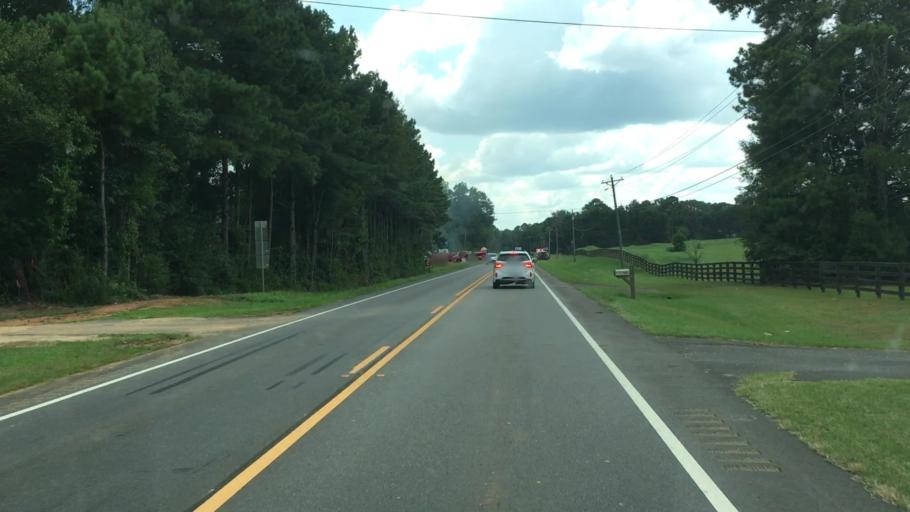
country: US
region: Georgia
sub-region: Putnam County
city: Eatonton
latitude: 33.3607
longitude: -83.3876
